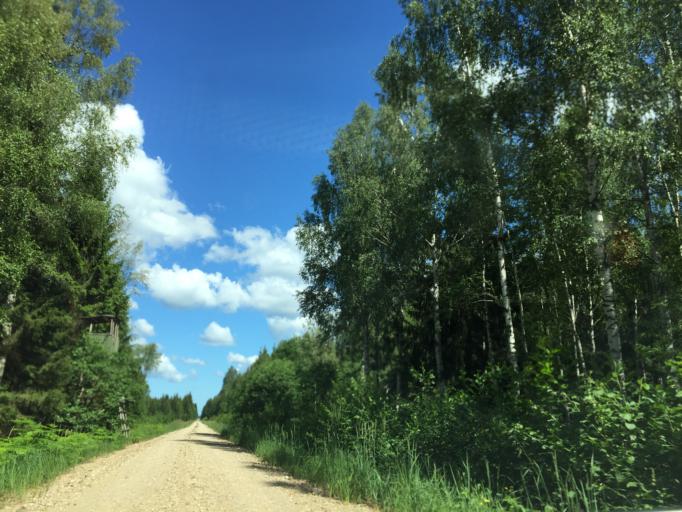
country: LV
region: Ventspils Rajons
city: Piltene
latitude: 57.2774
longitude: 21.8537
